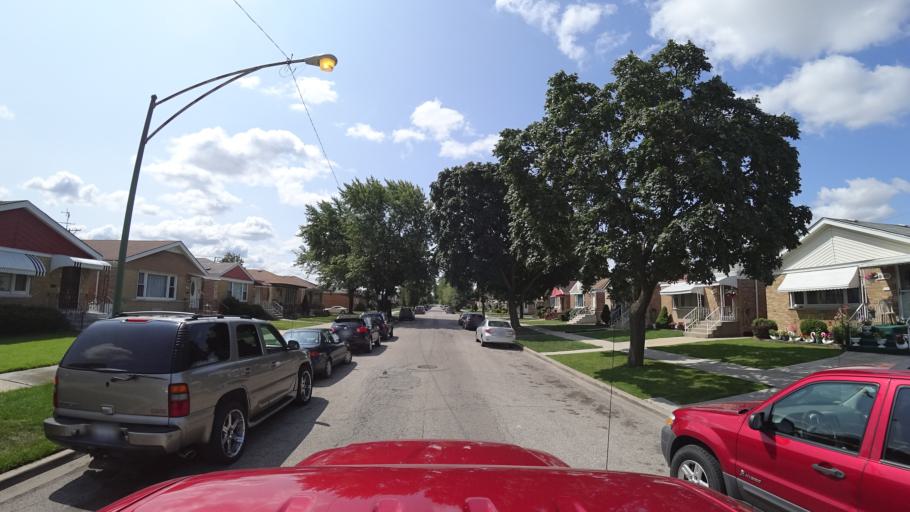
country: US
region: Illinois
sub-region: Cook County
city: Cicero
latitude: 41.8028
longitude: -87.7394
